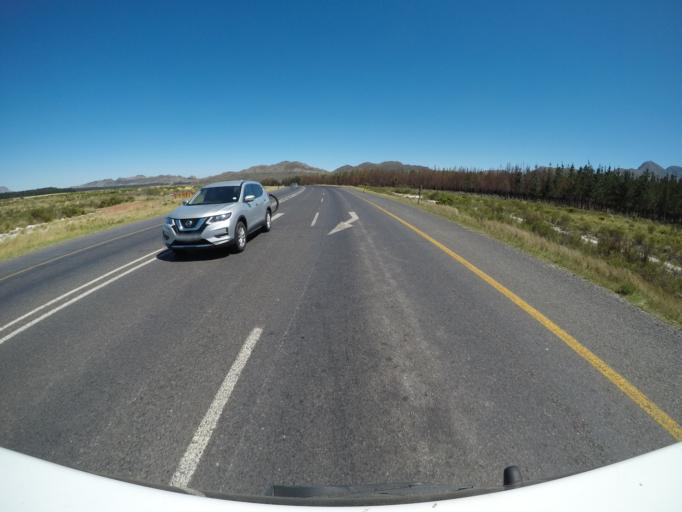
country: ZA
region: Western Cape
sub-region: Overberg District Municipality
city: Grabouw
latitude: -34.1534
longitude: 18.9672
